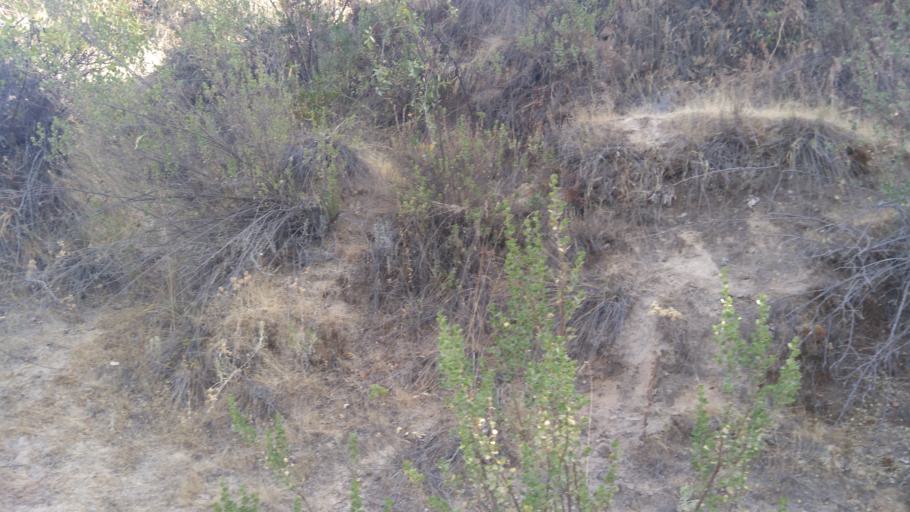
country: CL
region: Santiago Metropolitan
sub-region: Provincia de Cordillera
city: Puente Alto
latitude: -33.7260
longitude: -70.4746
